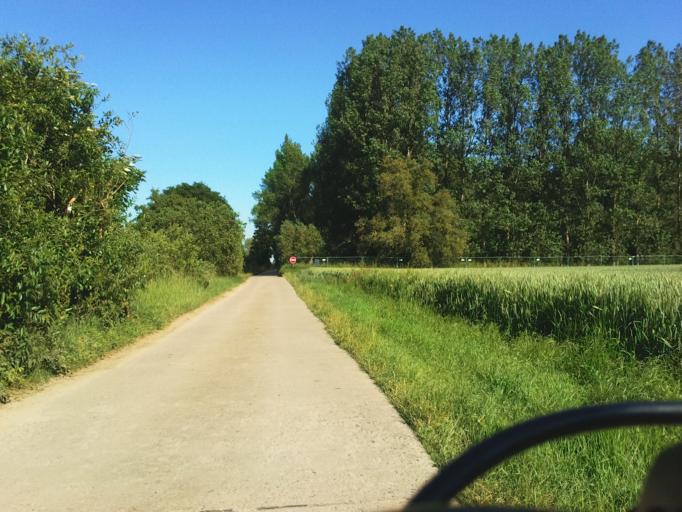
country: DE
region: Mecklenburg-Vorpommern
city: Monchhagen
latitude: 54.1659
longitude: 12.2107
